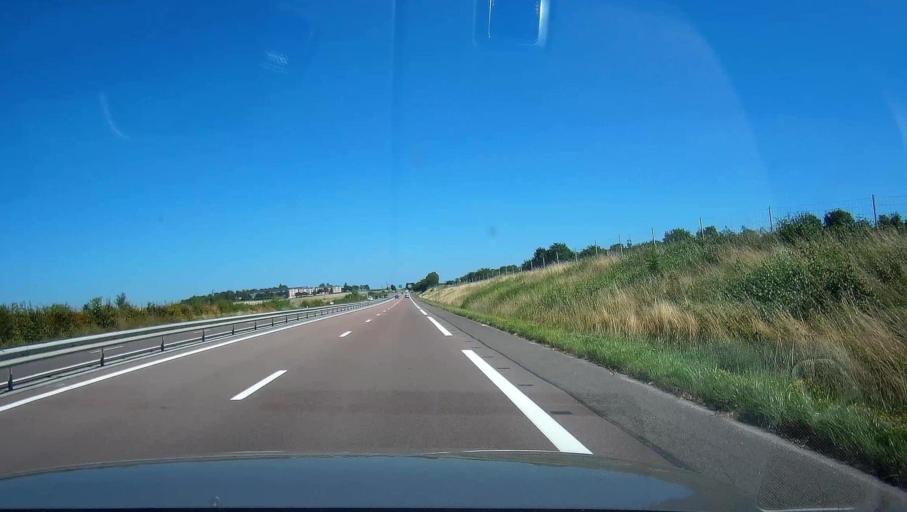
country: FR
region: Champagne-Ardenne
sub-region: Departement des Ardennes
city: Rethel
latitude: 49.5210
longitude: 4.3574
